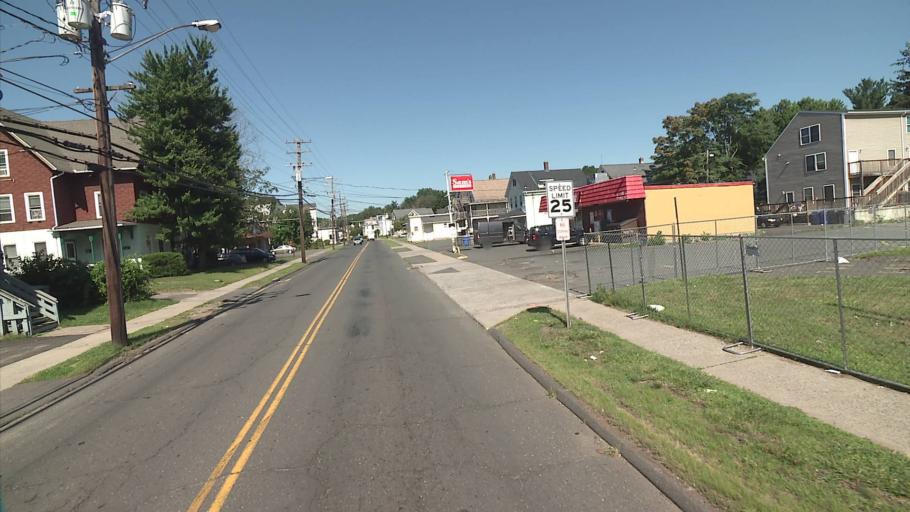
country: US
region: Connecticut
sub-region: Hartford County
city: Bristol
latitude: 41.6724
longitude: -72.9550
